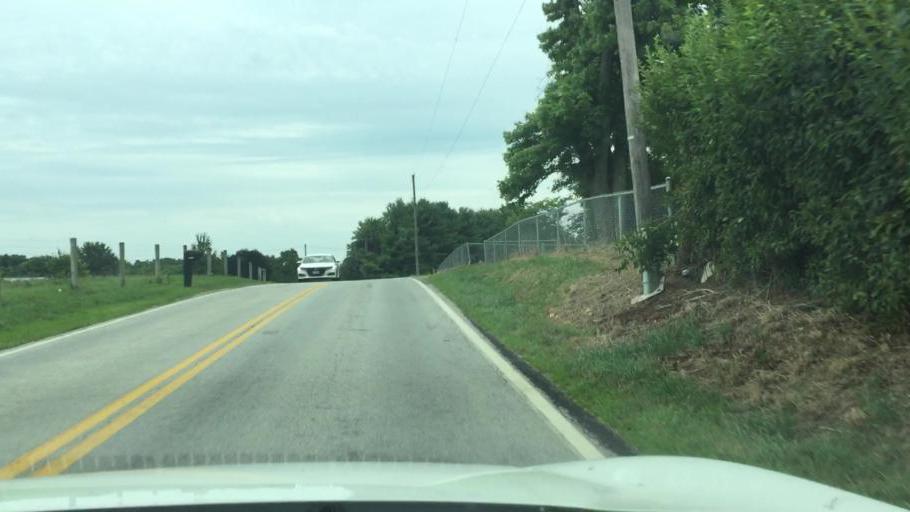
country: US
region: Ohio
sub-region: Clark County
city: Northridge
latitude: 39.9887
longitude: -83.6863
